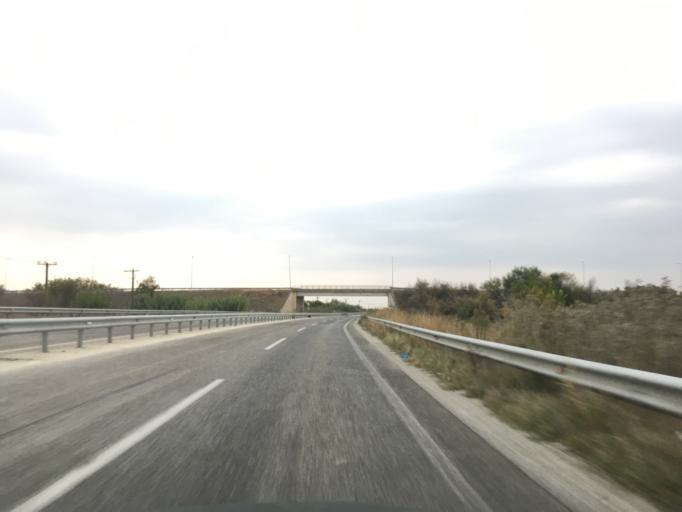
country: GR
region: Thessaly
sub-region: Trikala
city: Megalochori
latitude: 39.5668
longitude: 21.8441
